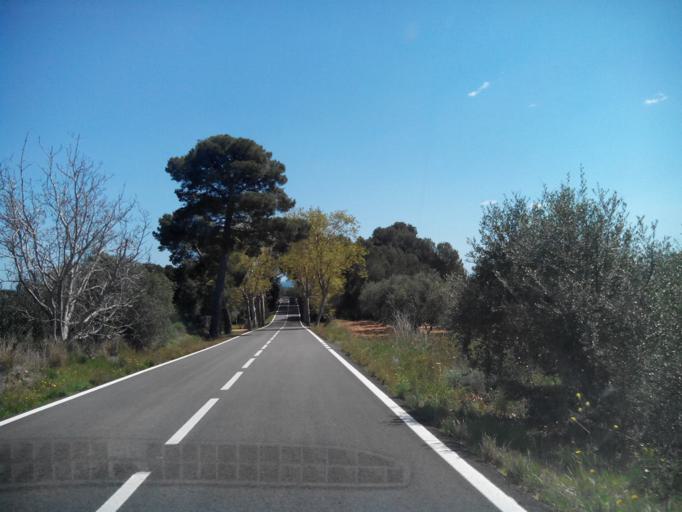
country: ES
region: Catalonia
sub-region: Provincia de Tarragona
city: Riudecanyes
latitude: 41.1024
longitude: 0.9632
